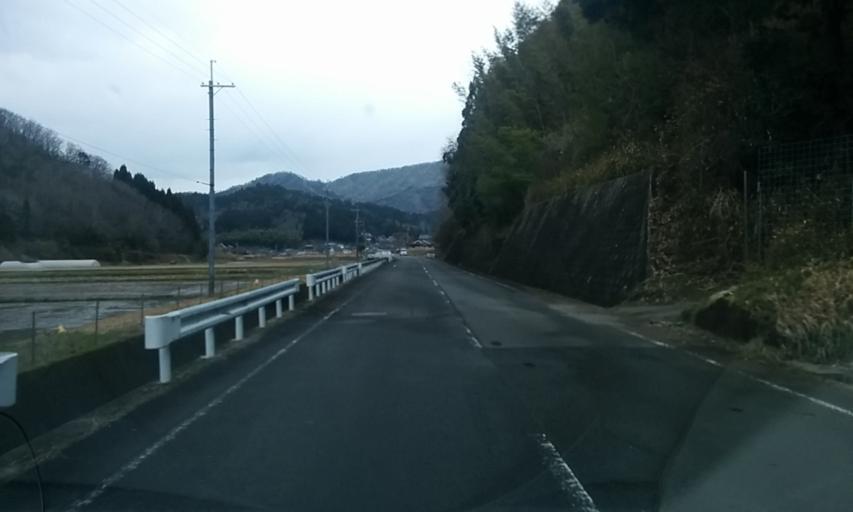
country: JP
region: Kyoto
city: Kameoka
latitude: 35.1220
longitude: 135.4180
